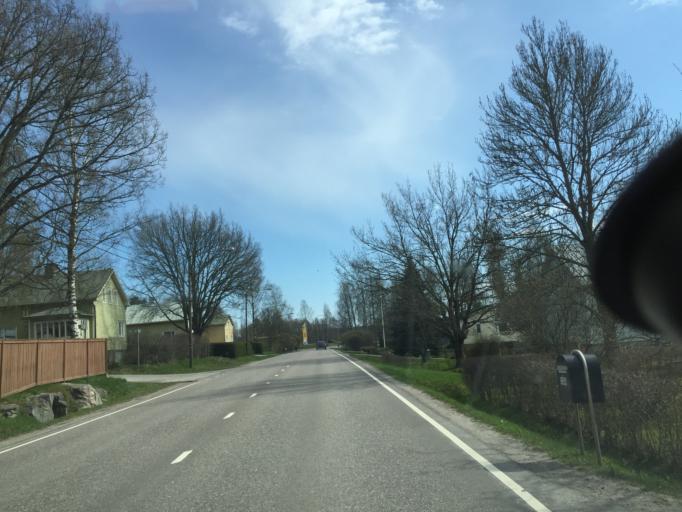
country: FI
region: Uusimaa
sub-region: Raaseporin
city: Ekenaes
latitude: 59.9869
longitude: 23.4171
